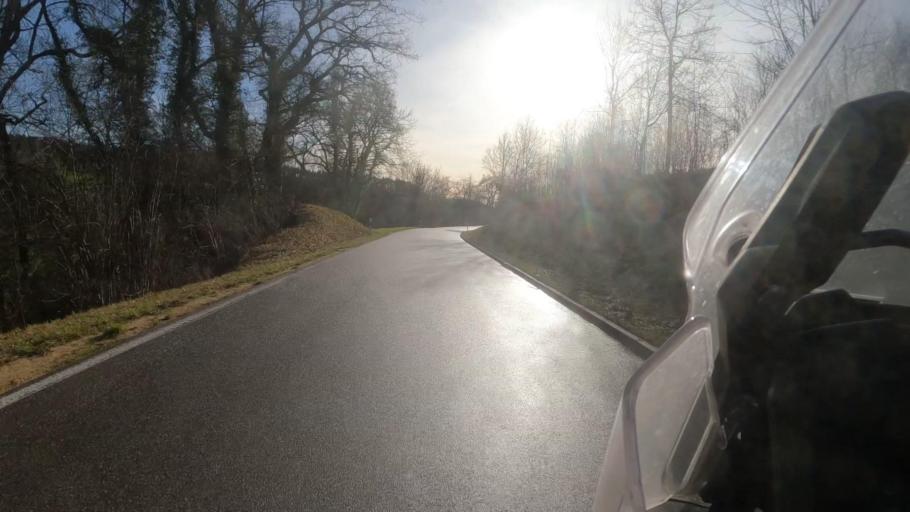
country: DE
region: Baden-Wuerttemberg
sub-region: Freiburg Region
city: Tengen
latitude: 47.8229
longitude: 8.6832
